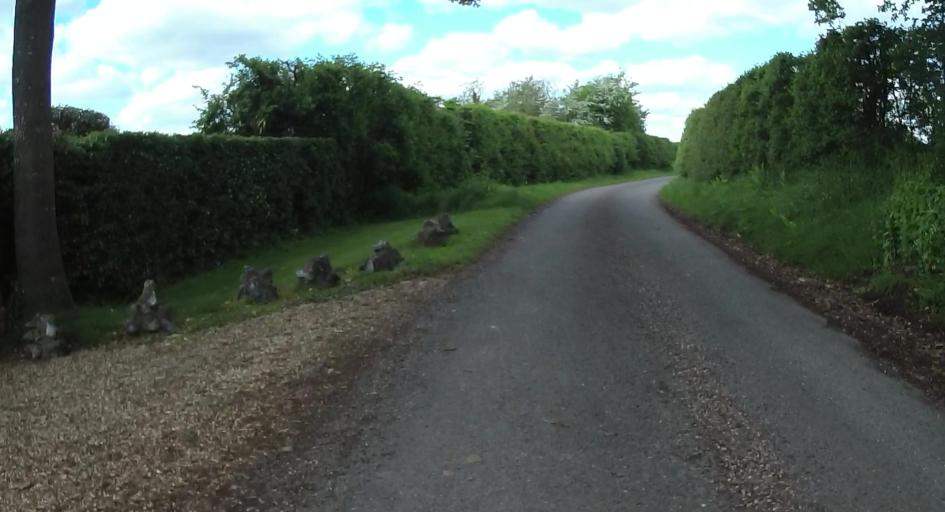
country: GB
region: England
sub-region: West Berkshire
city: Stratfield Mortimer
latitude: 51.3386
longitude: -1.0239
